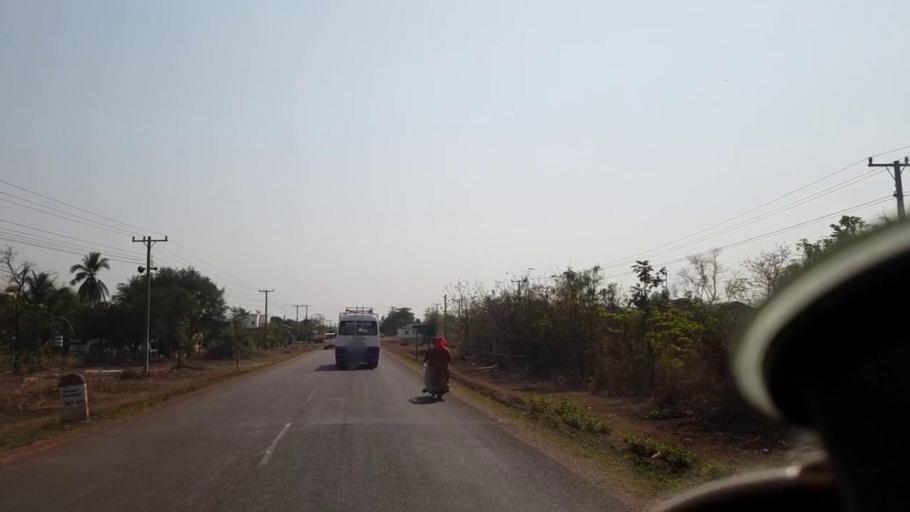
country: TH
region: Nong Khai
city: Nong Khai
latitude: 18.0551
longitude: 102.8326
